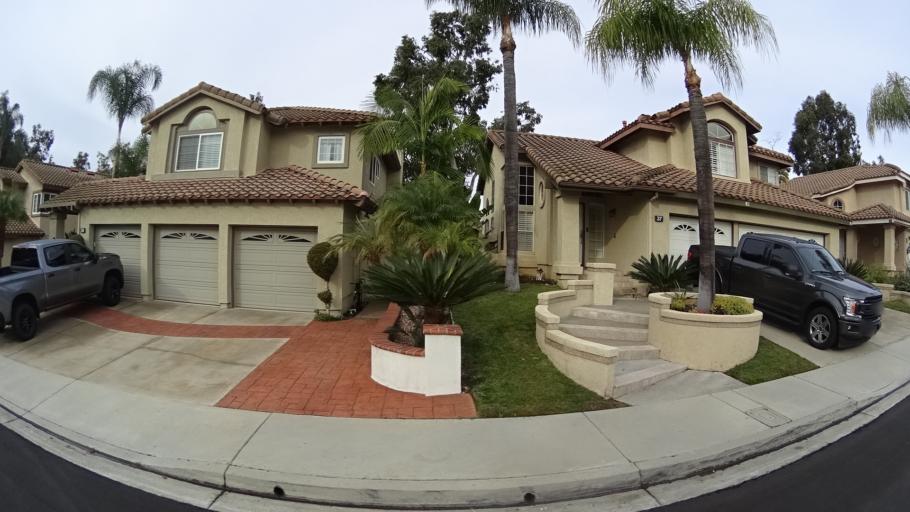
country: US
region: California
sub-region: Orange County
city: Las Flores
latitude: 33.6120
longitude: -117.6177
